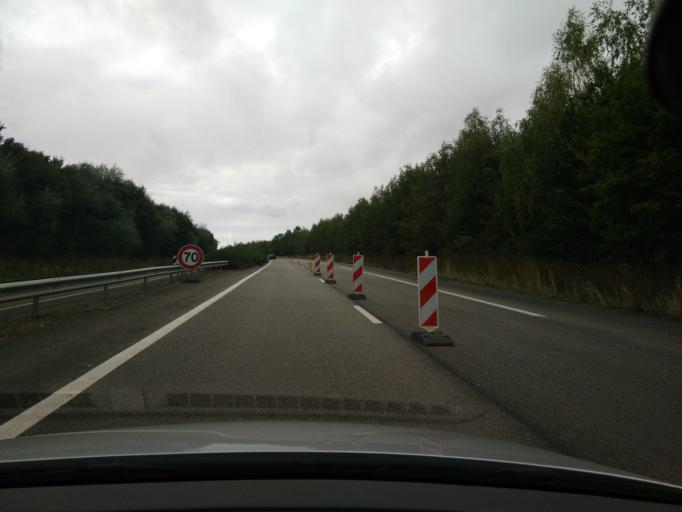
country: FR
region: Ile-de-France
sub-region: Departement des Yvelines
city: Houdan
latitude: 48.7829
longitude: 1.5825
